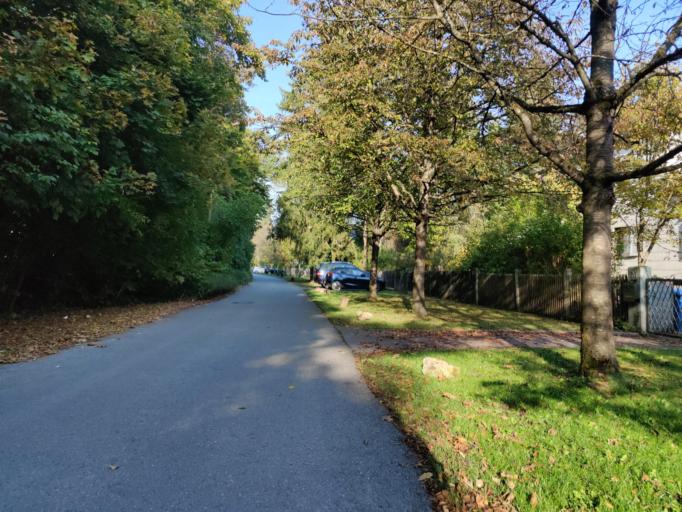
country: DE
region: Bavaria
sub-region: Upper Bavaria
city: Pasing
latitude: 48.1720
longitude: 11.4960
